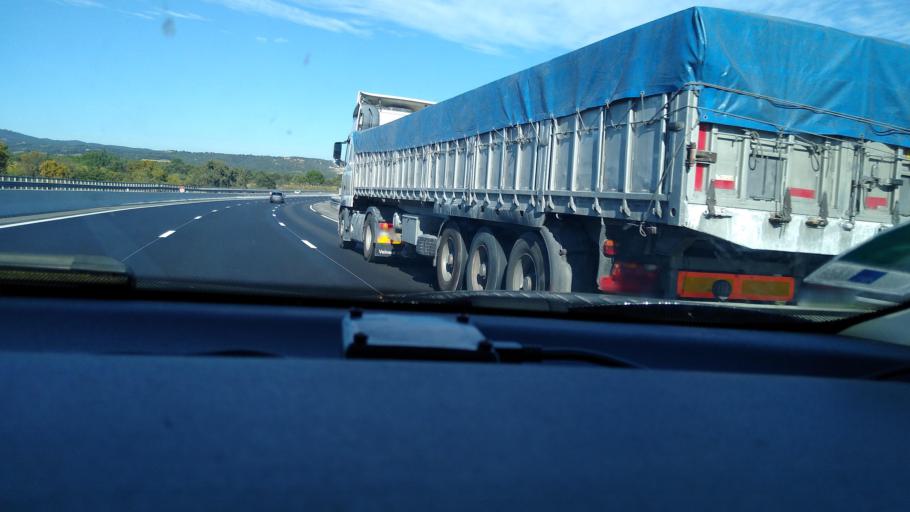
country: FR
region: Languedoc-Roussillon
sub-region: Departement des Pyrenees-Orientales
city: Maureillas-las-Illas
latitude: 42.4998
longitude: 2.8201
